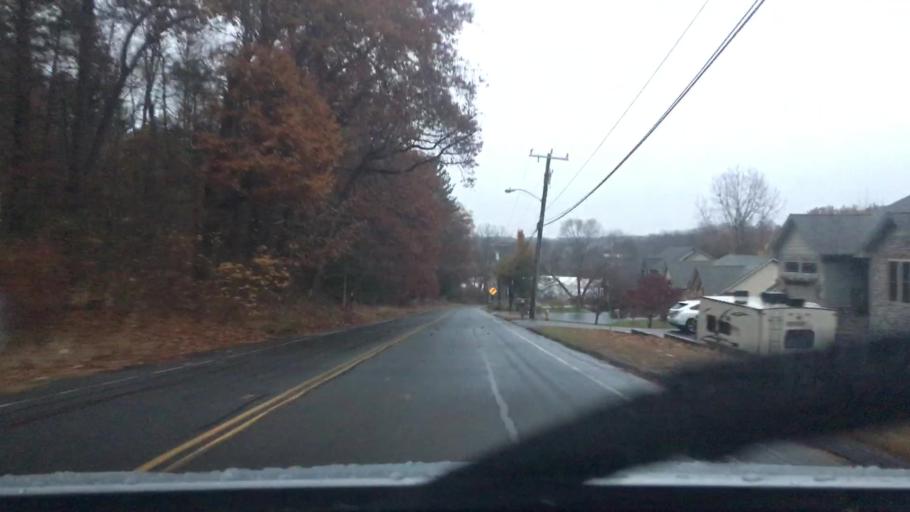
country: US
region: Massachusetts
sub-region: Hampden County
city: Southwick
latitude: 42.0632
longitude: -72.7053
